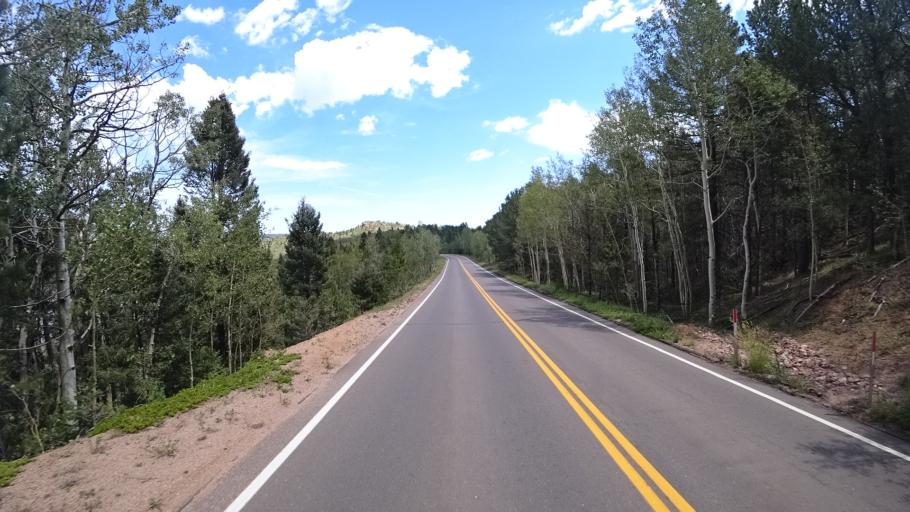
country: US
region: Colorado
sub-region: El Paso County
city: Cascade-Chipita Park
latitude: 38.9164
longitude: -105.0245
